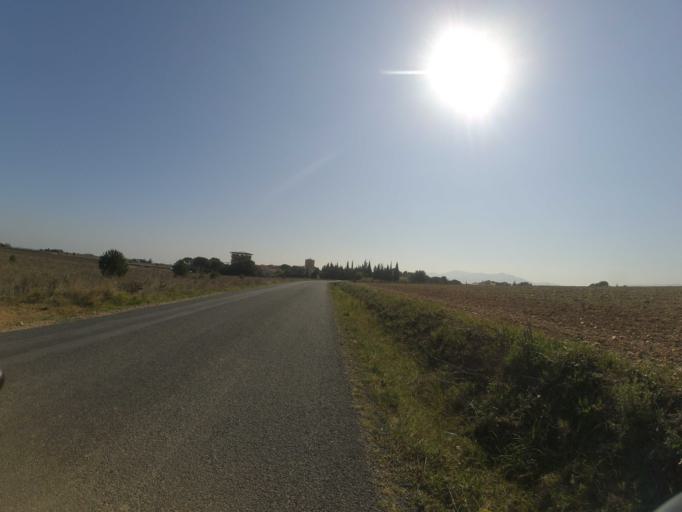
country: FR
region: Languedoc-Roussillon
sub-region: Departement des Pyrenees-Orientales
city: Llupia
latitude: 42.6100
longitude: 2.7662
